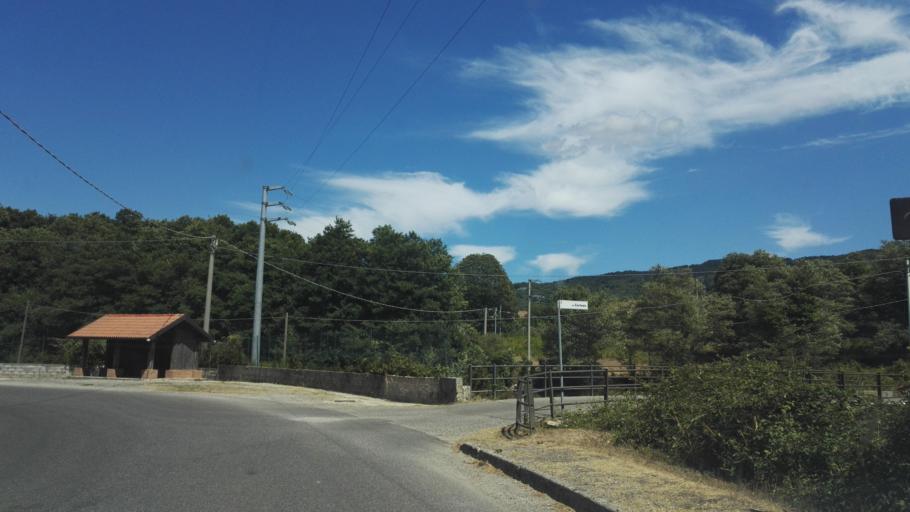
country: IT
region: Calabria
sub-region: Provincia di Vibo-Valentia
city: Serra San Bruno
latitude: 38.5651
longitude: 16.3285
